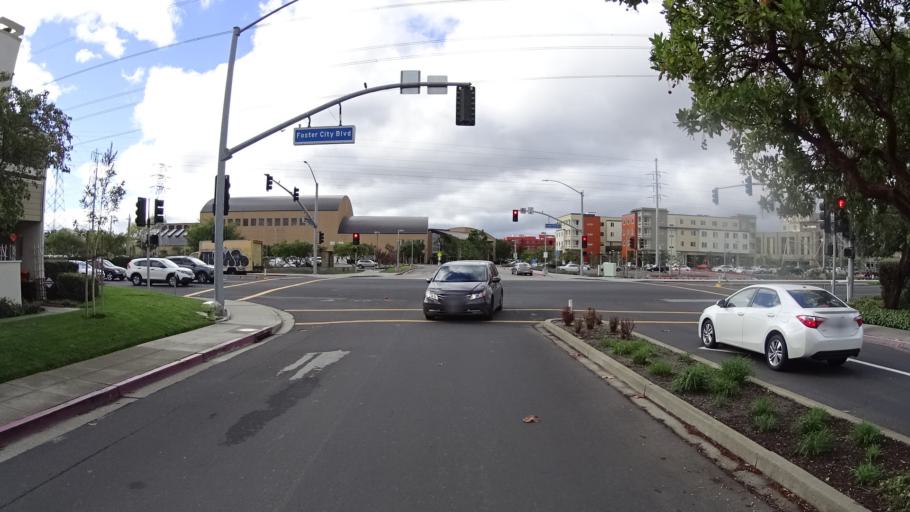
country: US
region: California
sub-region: San Mateo County
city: Foster City
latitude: 37.5599
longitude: -122.2657
